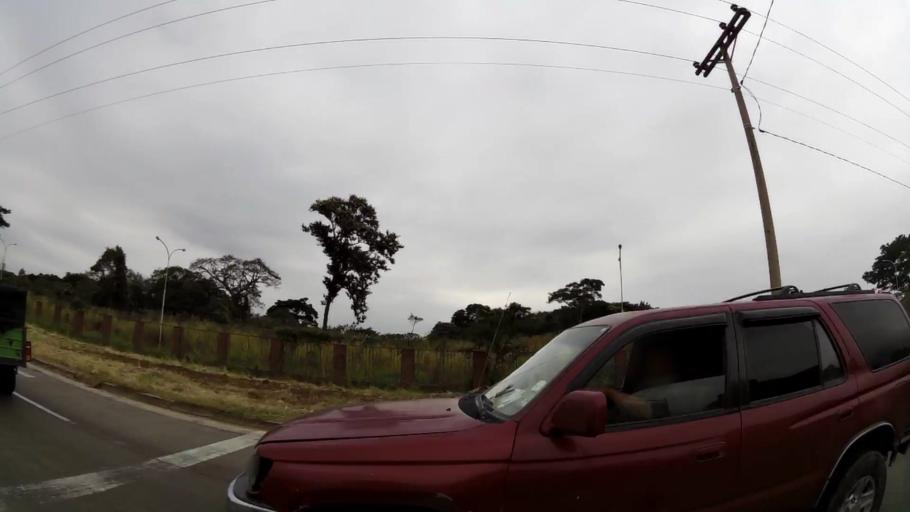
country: BO
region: Santa Cruz
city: Santa Cruz de la Sierra
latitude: -17.8331
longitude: -63.1875
